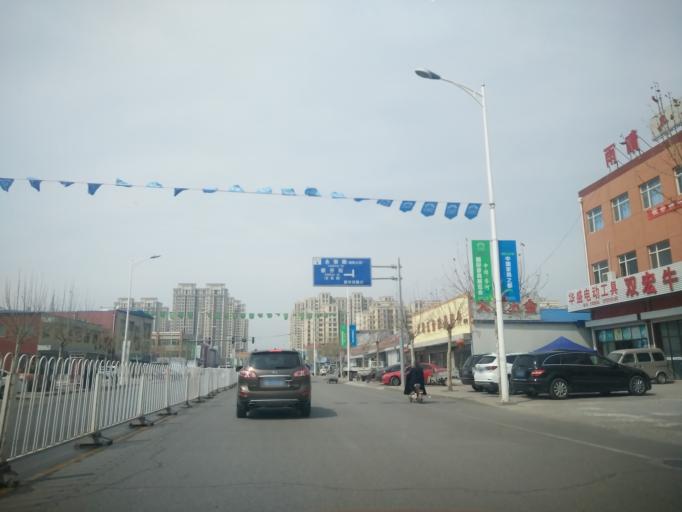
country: CN
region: Tianjin Shi
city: Xiawuqi
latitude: 39.7556
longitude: 117.0178
